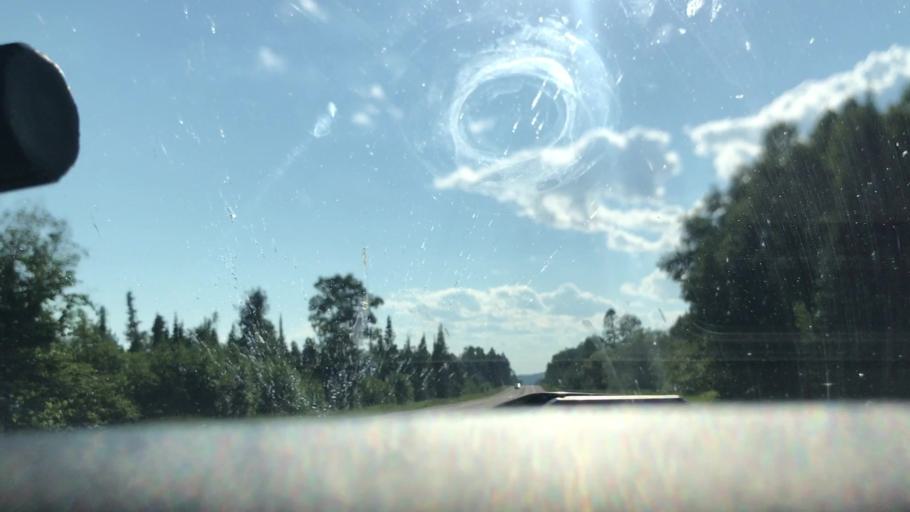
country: US
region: Minnesota
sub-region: Cook County
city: Grand Marais
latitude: 47.7971
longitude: -90.1189
